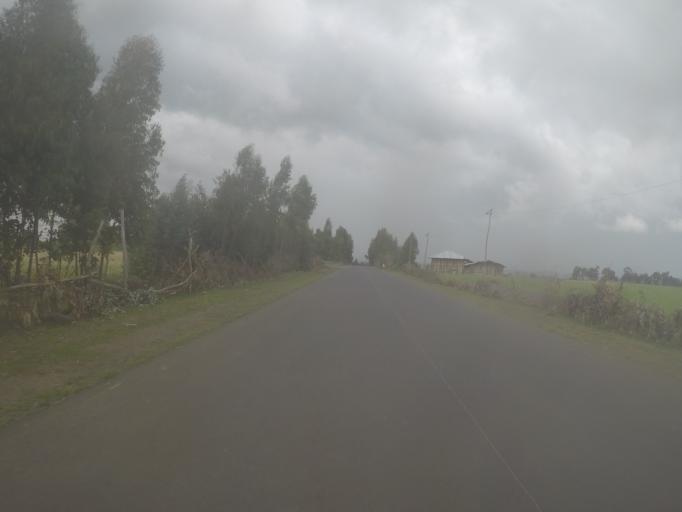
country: ET
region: Amhara
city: Dabat
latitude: 12.9430
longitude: 37.7454
